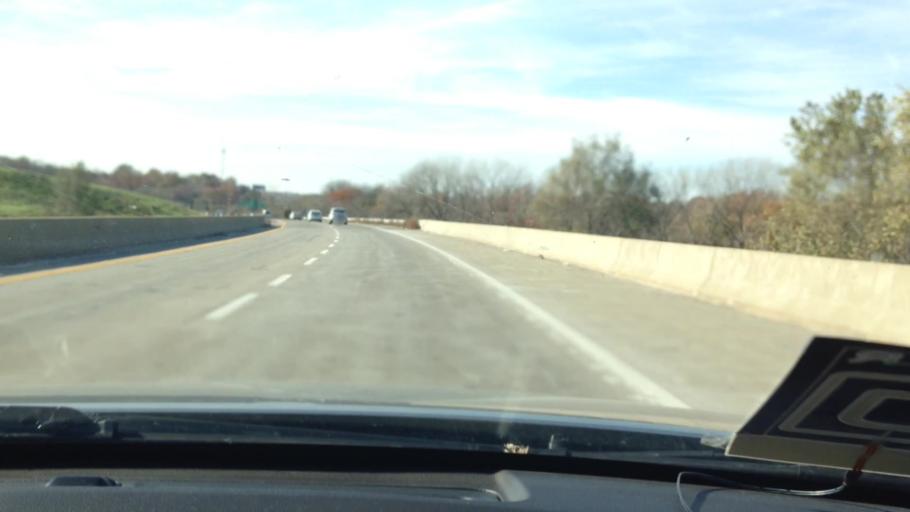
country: US
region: Missouri
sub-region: Platte County
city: Riverside
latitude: 39.1844
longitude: -94.5920
